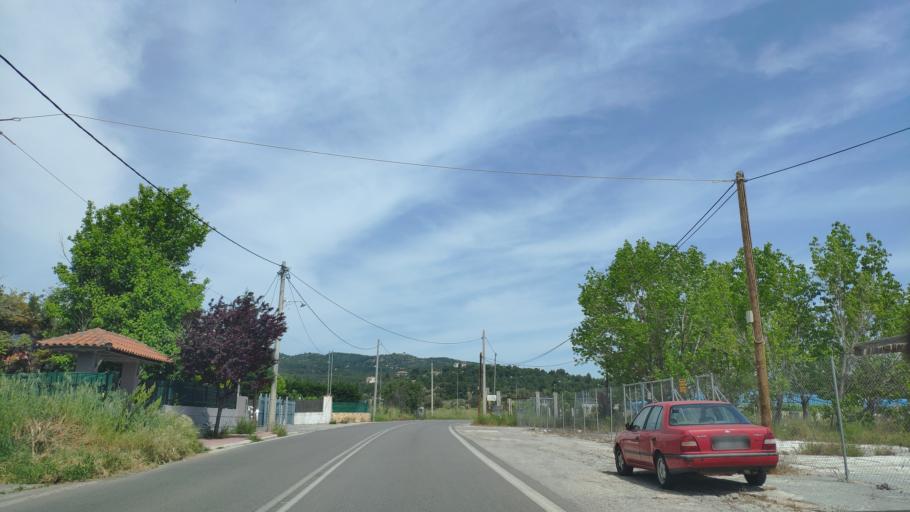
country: GR
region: Attica
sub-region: Nomarchia Anatolikis Attikis
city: Afidnes
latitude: 38.1945
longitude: 23.8532
